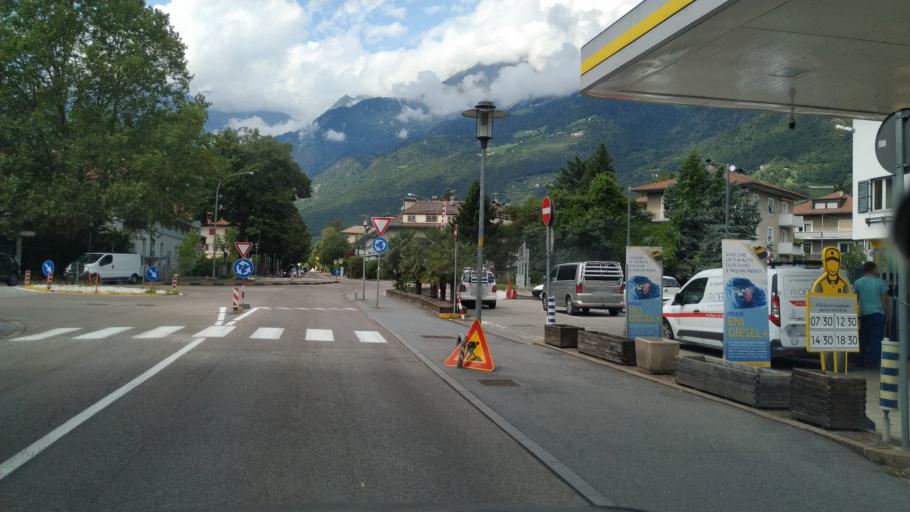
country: IT
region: Trentino-Alto Adige
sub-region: Bolzano
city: Merano
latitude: 46.6768
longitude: 11.1492
